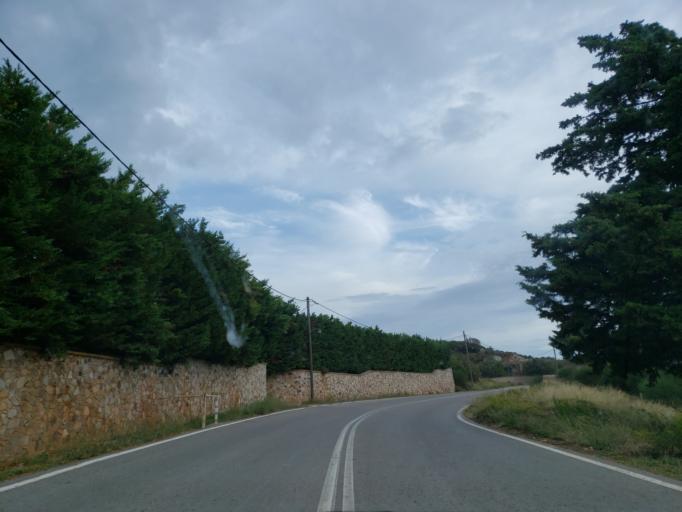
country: GR
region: Attica
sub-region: Nomarchia Anatolikis Attikis
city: Varnavas
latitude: 38.2185
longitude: 23.9395
